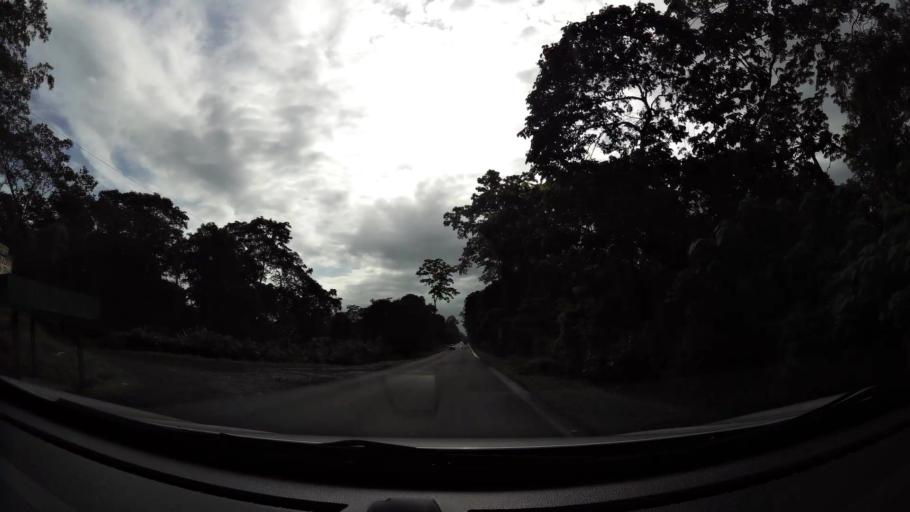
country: CR
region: Limon
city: Pocora
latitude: 10.1927
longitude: -83.6409
